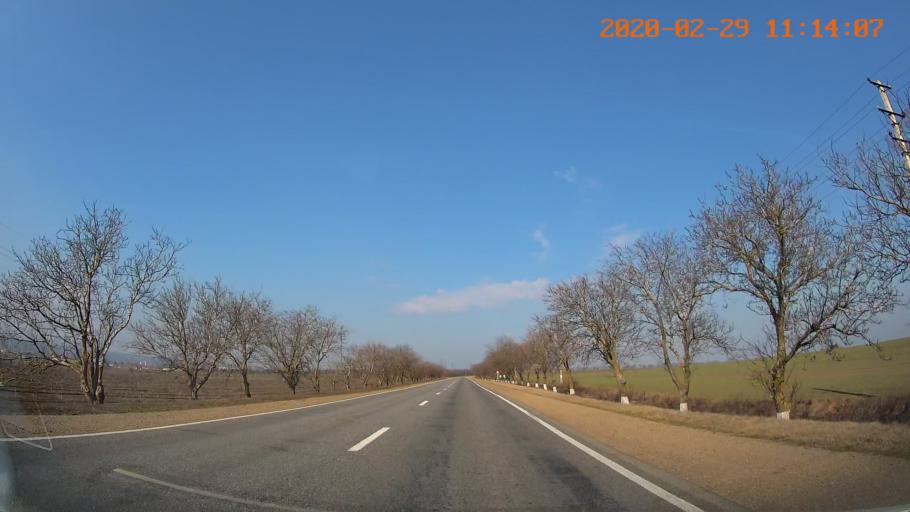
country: MD
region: Telenesti
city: Dubasari
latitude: 47.2789
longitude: 29.1759
